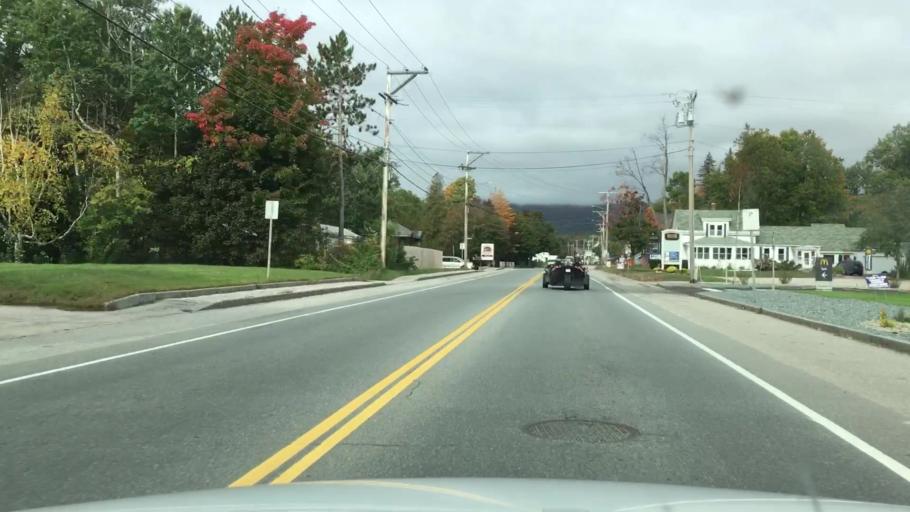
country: US
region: New Hampshire
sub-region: Coos County
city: Gorham
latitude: 44.3923
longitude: -71.1864
